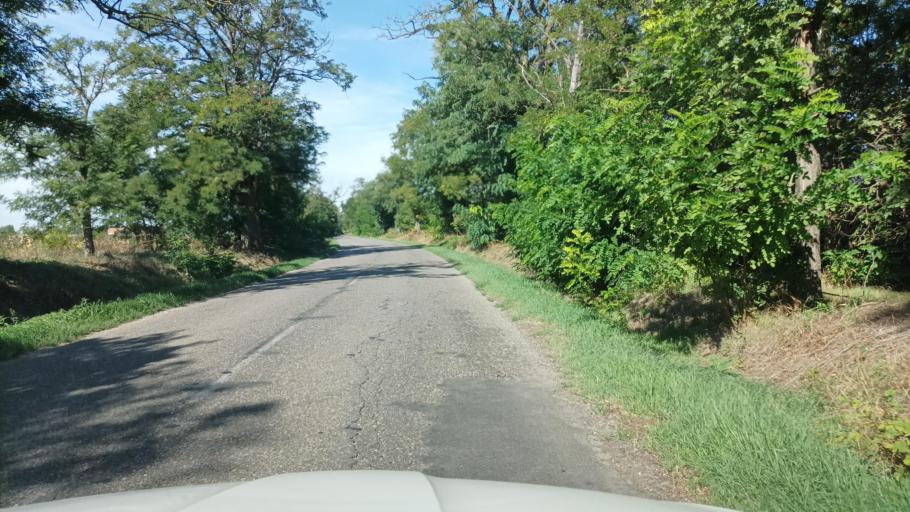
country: HU
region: Pest
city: Vacszentlaszlo
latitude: 47.5594
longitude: 19.5639
